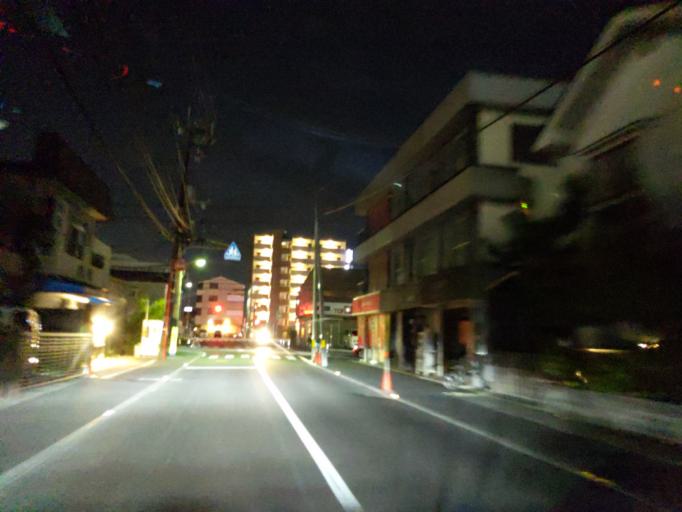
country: JP
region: Okayama
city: Okayama-shi
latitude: 34.6822
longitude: 133.9112
